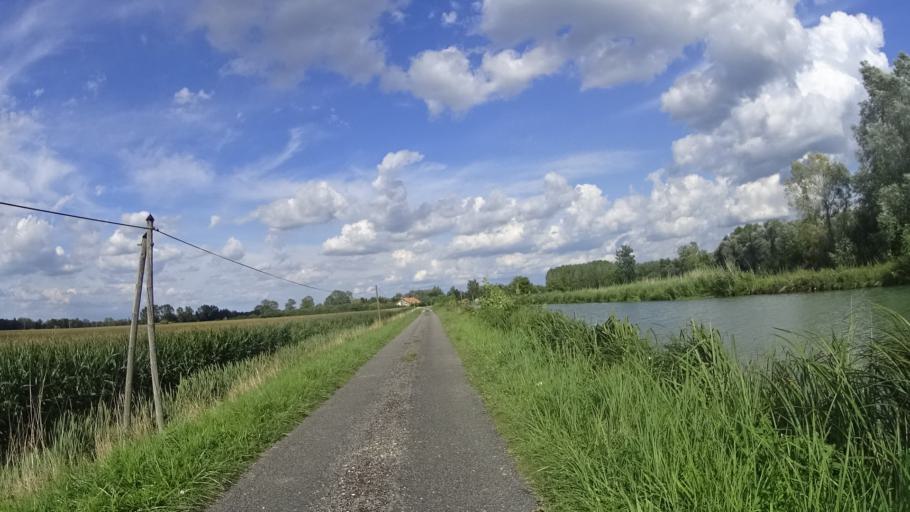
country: FR
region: Champagne-Ardenne
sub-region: Departement de la Marne
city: Sermaize-les-Bains
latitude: 48.7882
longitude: 4.8903
